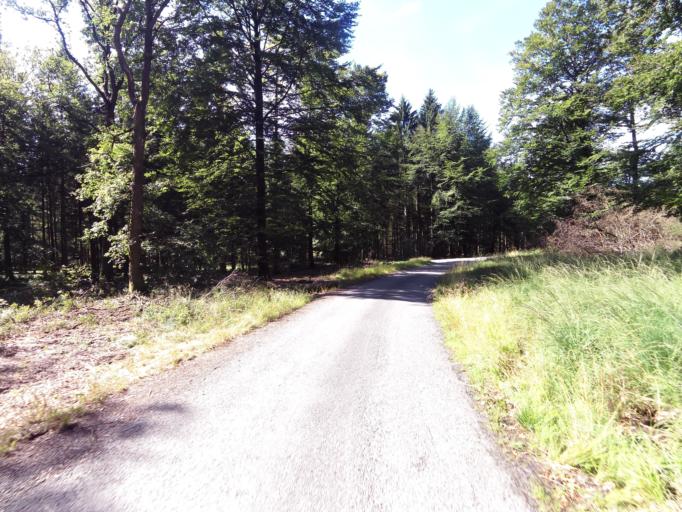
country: BE
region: Wallonia
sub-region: Province du Luxembourg
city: Nassogne
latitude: 50.1062
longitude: 5.3821
